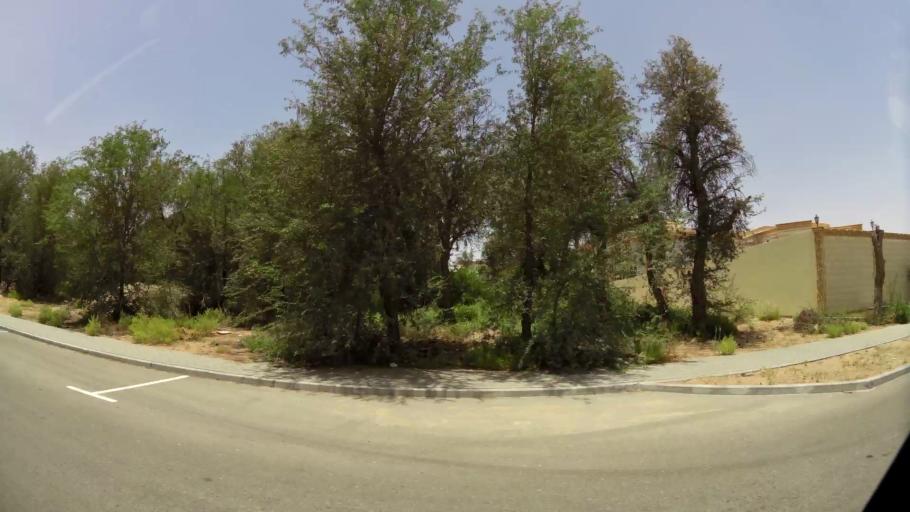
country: OM
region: Al Buraimi
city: Al Buraymi
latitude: 24.2818
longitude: 55.7359
